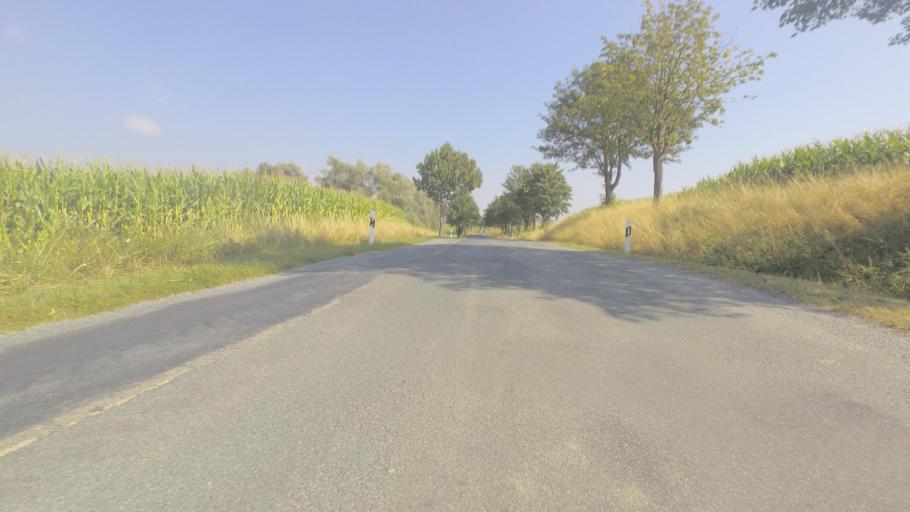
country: DE
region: Mecklenburg-Vorpommern
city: Pampow
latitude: 53.7058
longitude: 12.6156
